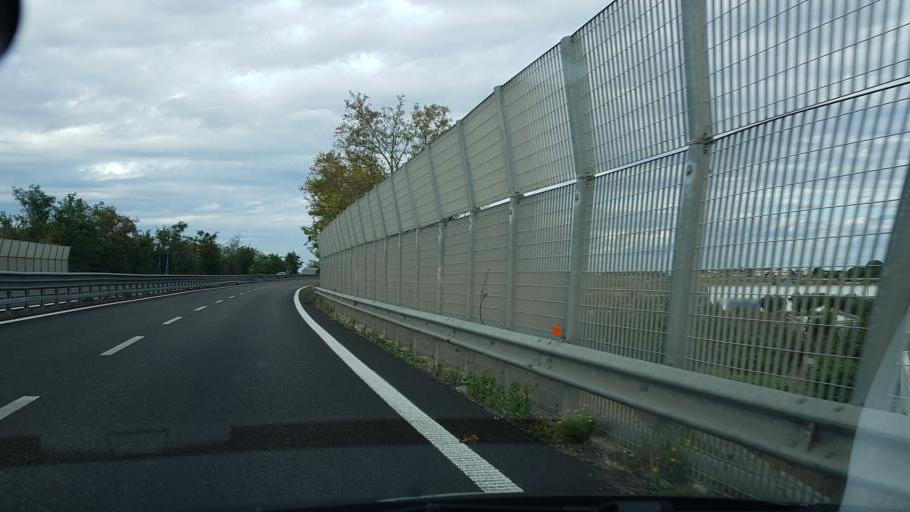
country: IT
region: Apulia
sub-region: Provincia di Lecce
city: Castromediano
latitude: 40.3256
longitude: 18.1854
